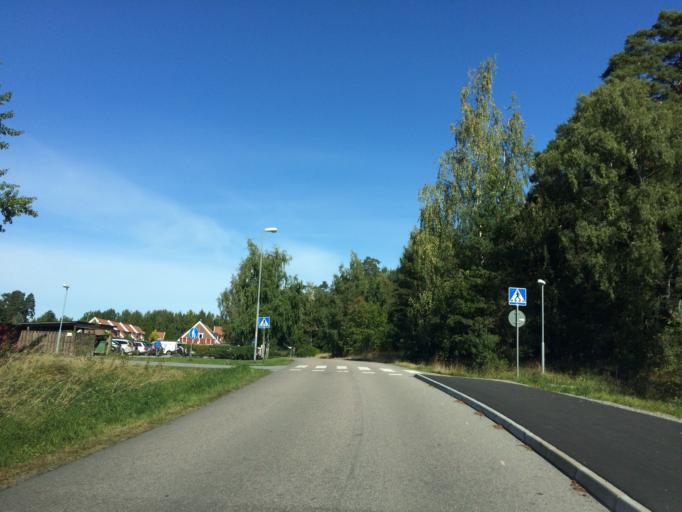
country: SE
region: Stockholm
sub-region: Sollentuna Kommun
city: Sollentuna
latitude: 59.4070
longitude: 17.9851
